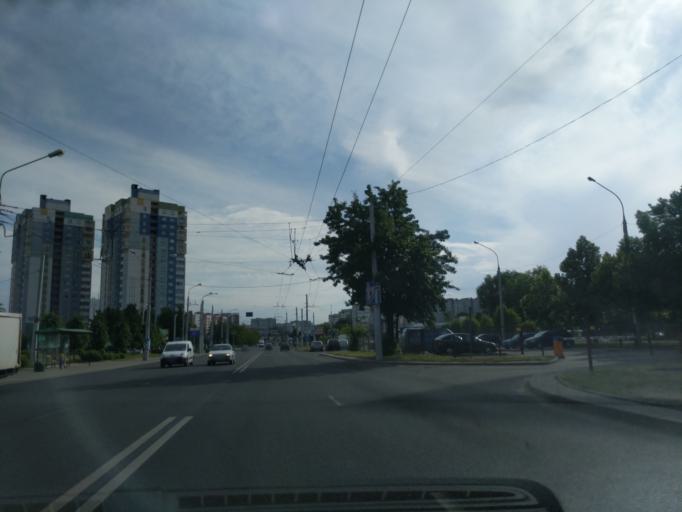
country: BY
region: Minsk
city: Novoye Medvezhino
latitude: 53.8668
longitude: 27.4706
